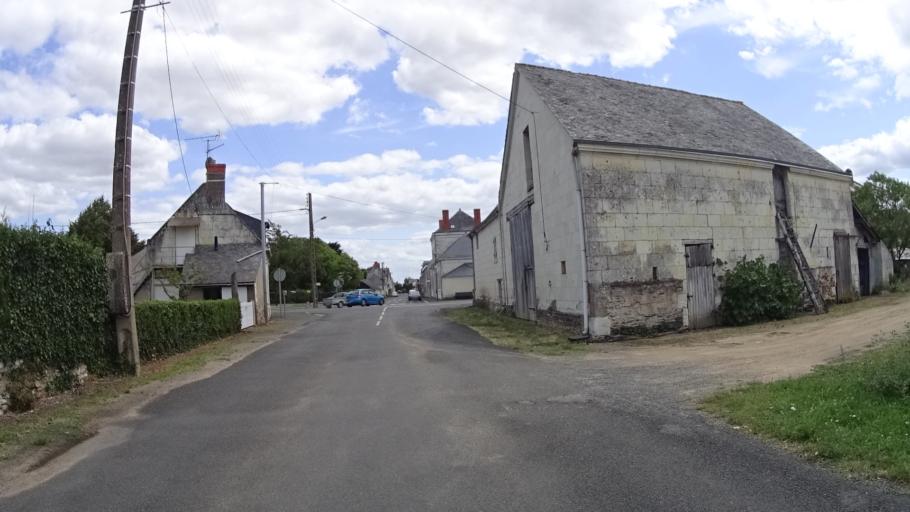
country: FR
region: Pays de la Loire
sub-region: Departement de Maine-et-Loire
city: La Menitre
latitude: 47.4034
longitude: -0.2714
